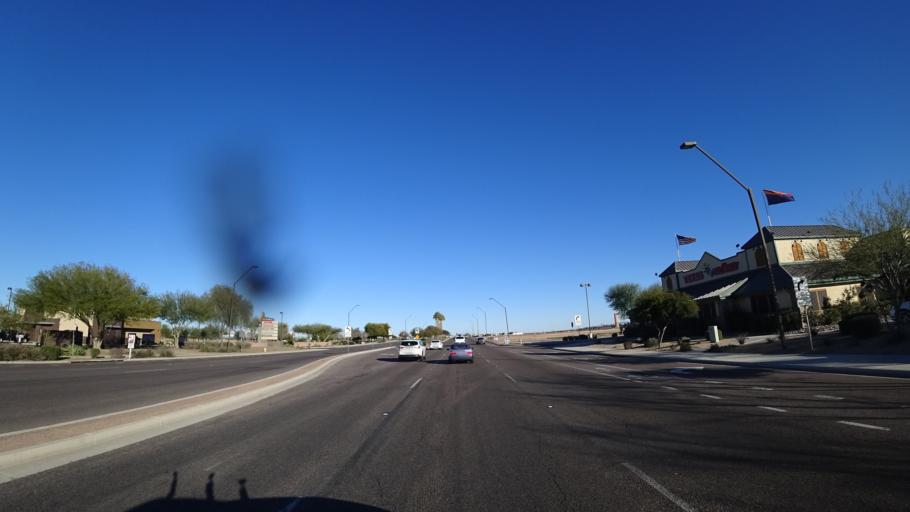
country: US
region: Arizona
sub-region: Maricopa County
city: Goodyear
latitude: 33.4644
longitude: -112.3876
